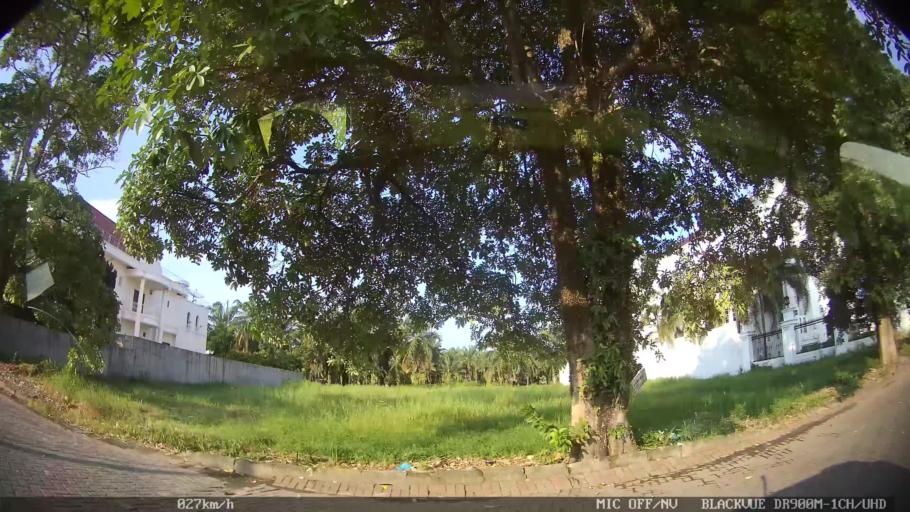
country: ID
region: North Sumatra
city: Medan
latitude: 3.6218
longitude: 98.6494
